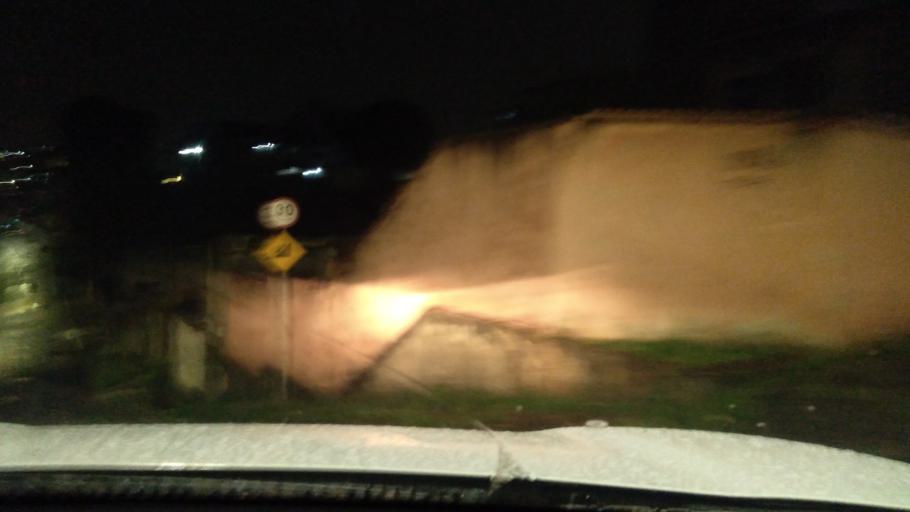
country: BR
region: Minas Gerais
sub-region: Belo Horizonte
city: Belo Horizonte
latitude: -19.9004
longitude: -43.9595
